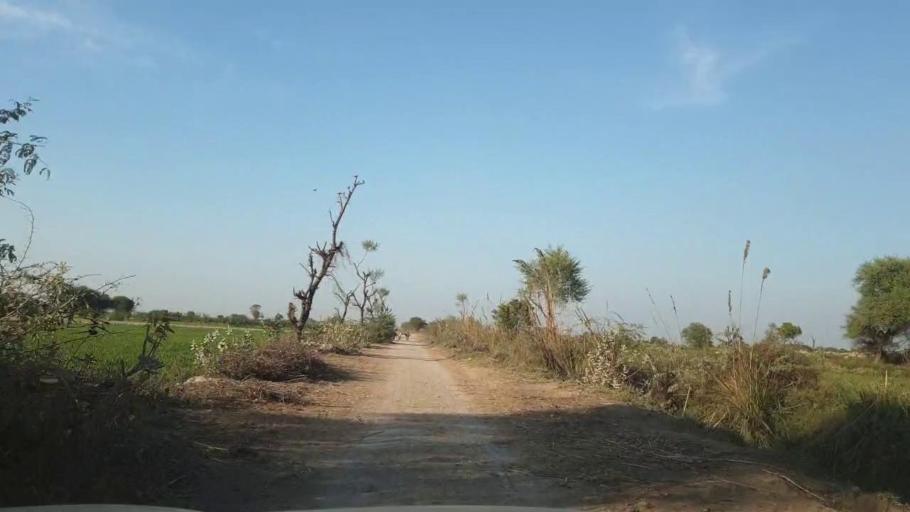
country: PK
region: Sindh
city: Tando Adam
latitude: 25.6993
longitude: 68.7023
